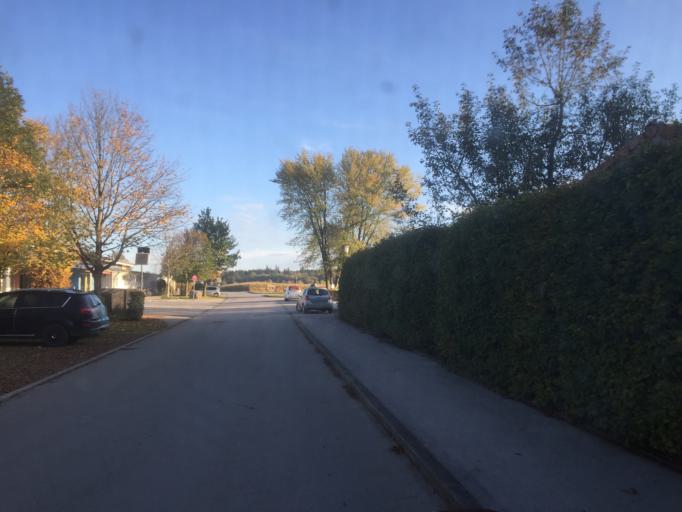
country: DE
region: Bavaria
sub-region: Upper Bavaria
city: Chieming
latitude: 47.8986
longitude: 12.5387
